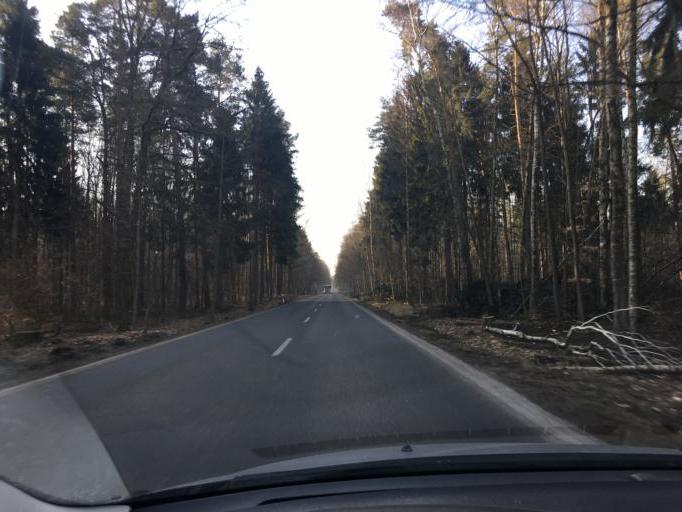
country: DE
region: Thuringia
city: Langenleuba-Niederhain
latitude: 50.9897
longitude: 12.5641
